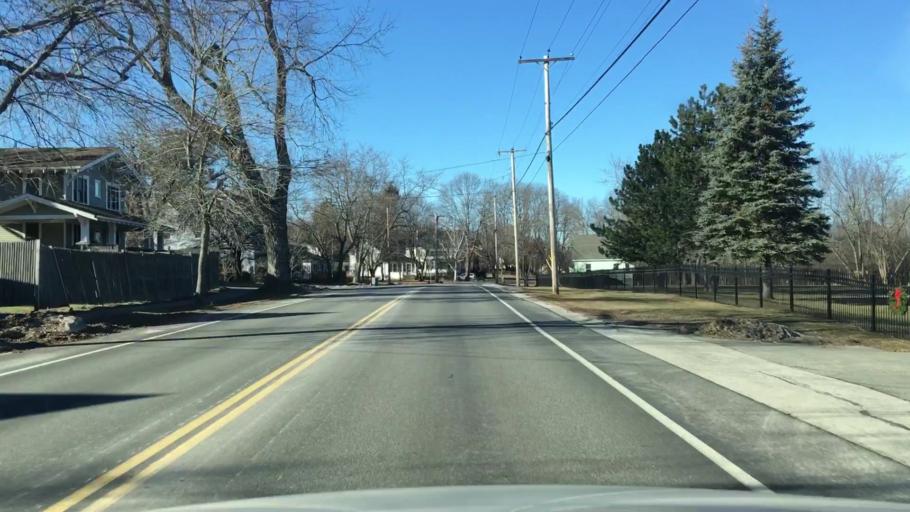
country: US
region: Maine
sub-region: Penobscot County
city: Bangor
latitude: 44.8126
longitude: -68.7937
